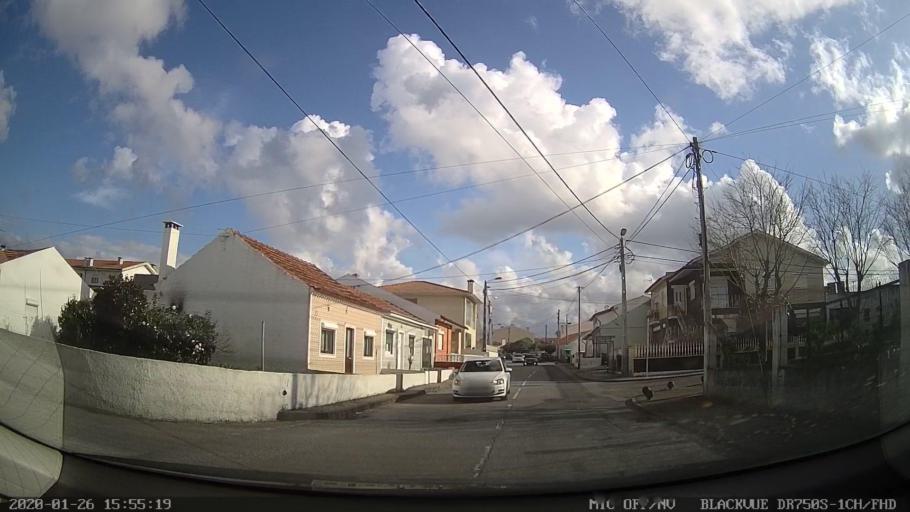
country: PT
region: Aveiro
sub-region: Aveiro
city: Aradas
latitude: 40.6283
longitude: -8.6276
